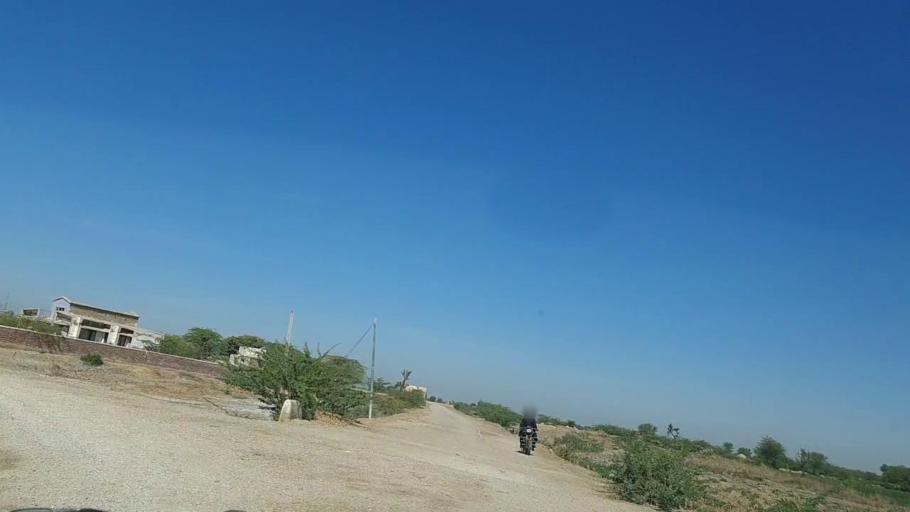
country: PK
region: Sindh
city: Dhoro Naro
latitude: 25.4862
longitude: 69.5272
